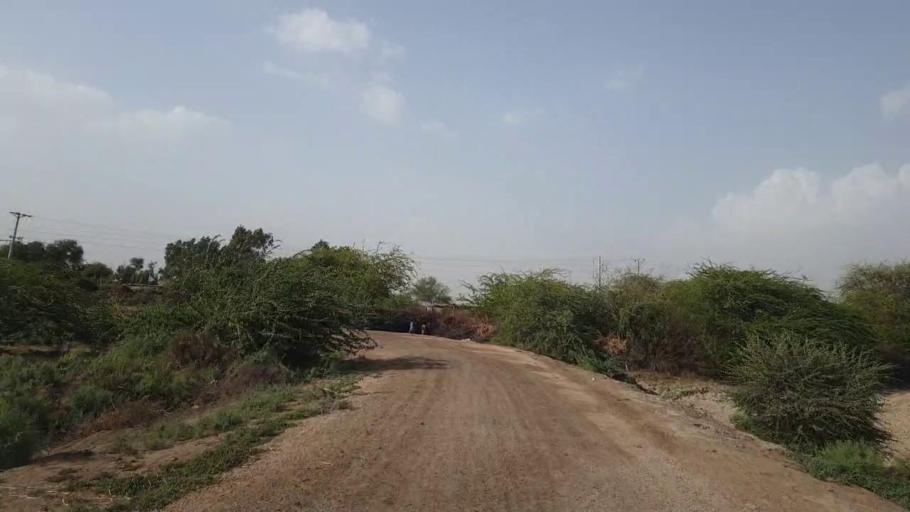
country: PK
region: Sindh
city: Tando Ghulam Ali
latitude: 25.1010
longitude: 68.8629
